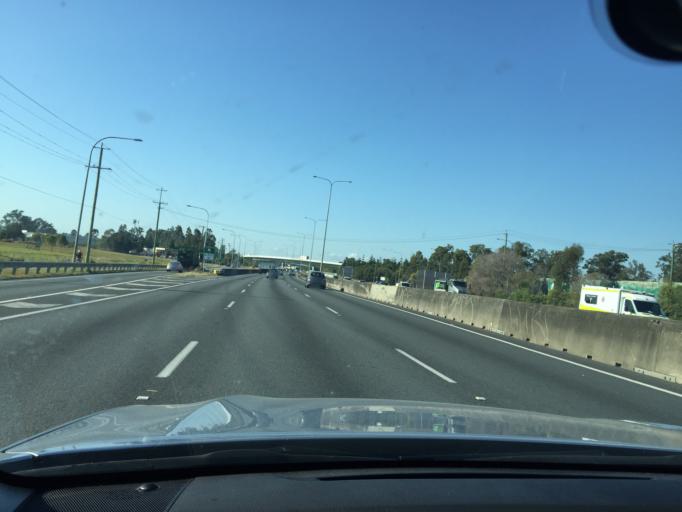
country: AU
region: Queensland
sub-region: Logan
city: Beenleigh
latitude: -27.6818
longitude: 153.1876
